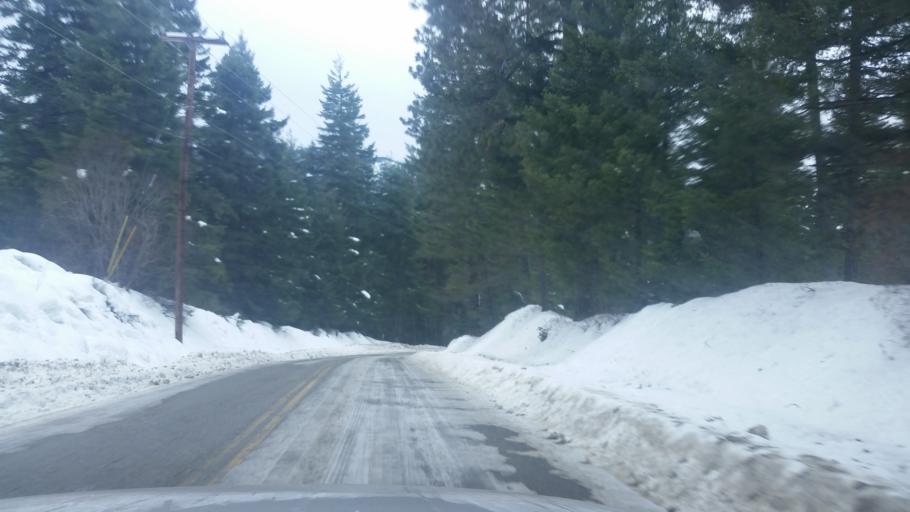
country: US
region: Washington
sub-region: Kittitas County
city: Cle Elum
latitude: 47.1688
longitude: -120.9767
